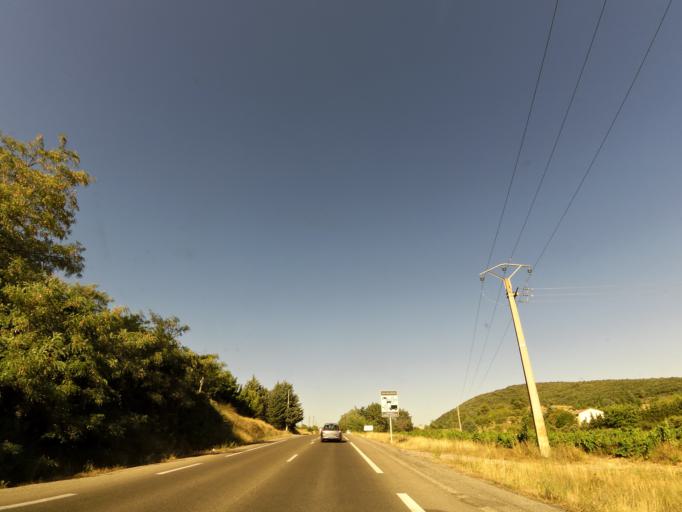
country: FR
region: Languedoc-Roussillon
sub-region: Departement du Gard
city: Saint-Hippolyte-du-Fort
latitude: 43.9534
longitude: 3.8043
